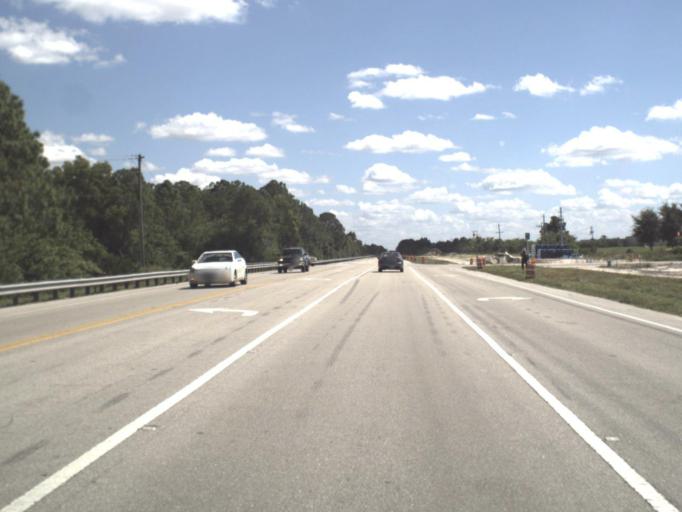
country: US
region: Florida
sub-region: Collier County
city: Lely Resort
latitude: 26.0355
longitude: -81.6557
